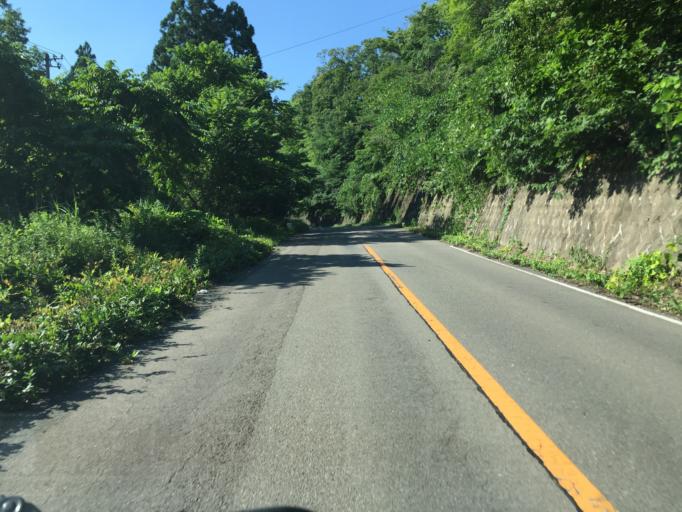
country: JP
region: Fukushima
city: Fukushima-shi
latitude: 37.8533
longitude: 140.4372
